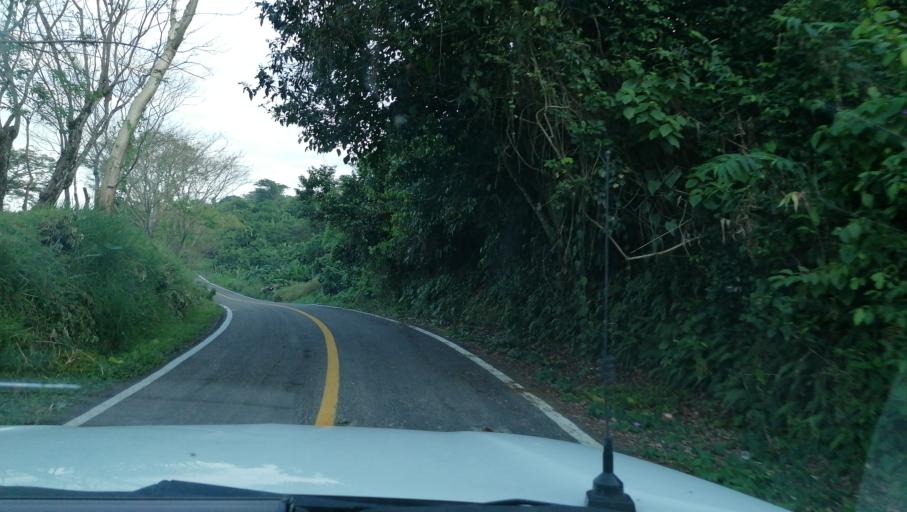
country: MX
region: Chiapas
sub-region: Juarez
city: El Triunfo 1ra. Seccion (Cardona)
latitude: 17.5069
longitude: -93.2292
